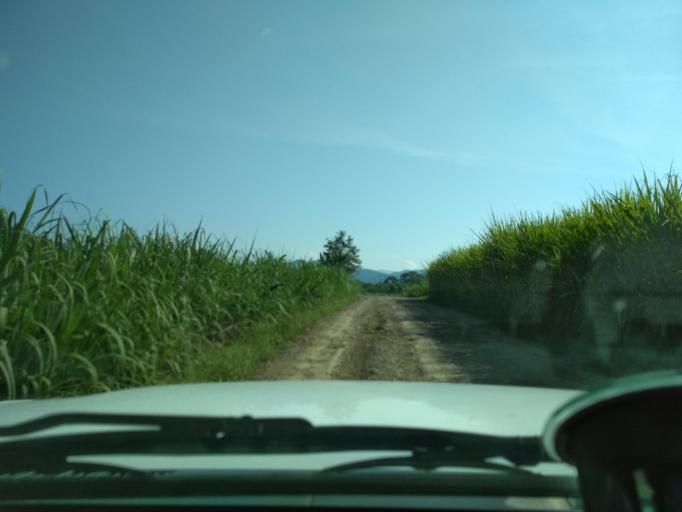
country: MX
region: Veracruz
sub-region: Chocaman
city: San Jose Neria
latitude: 18.9880
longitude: -97.0050
